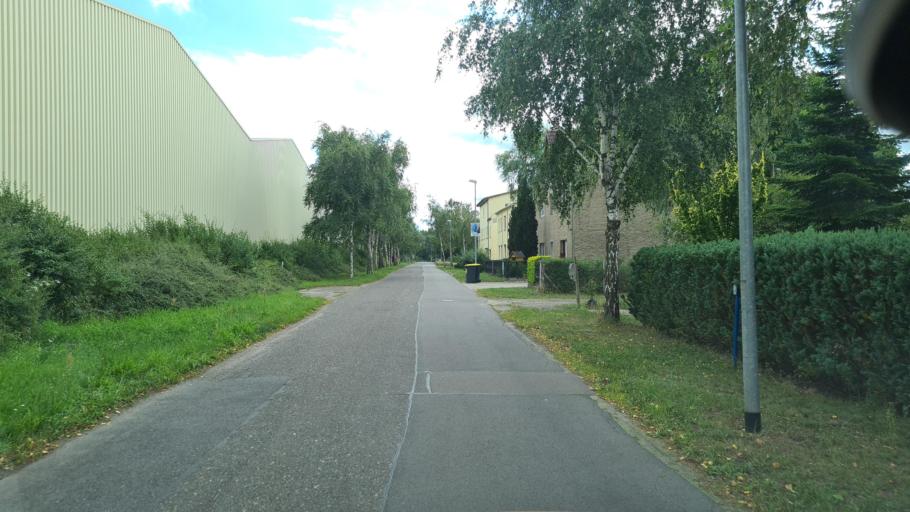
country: DE
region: Brandenburg
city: Drebkau
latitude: 51.6512
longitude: 14.2239
